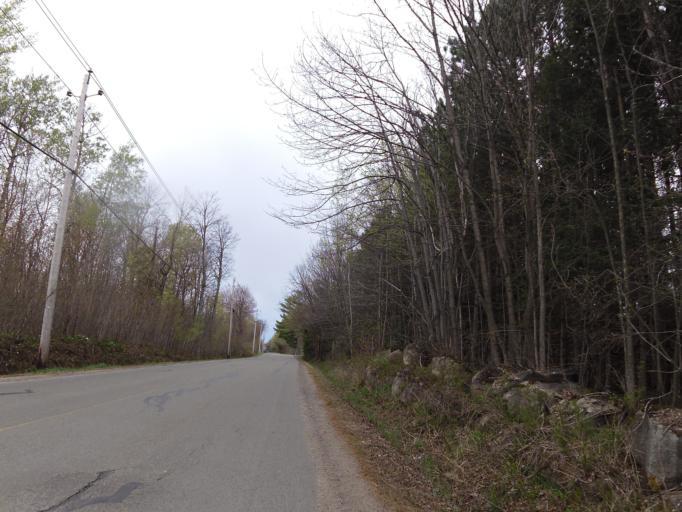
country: CA
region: Ontario
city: Hawkesbury
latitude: 45.6236
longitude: -74.5681
